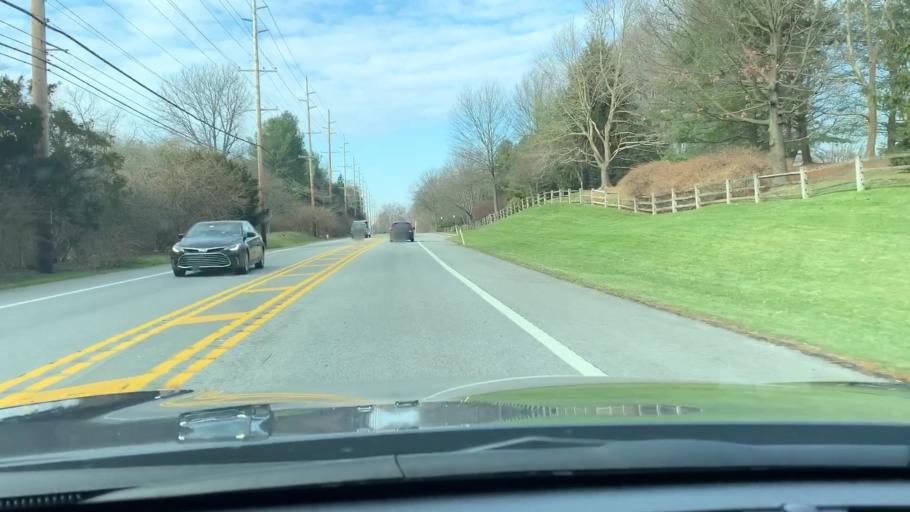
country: US
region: Pennsylvania
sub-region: Chester County
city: Berwyn
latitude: 40.0176
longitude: -75.4431
